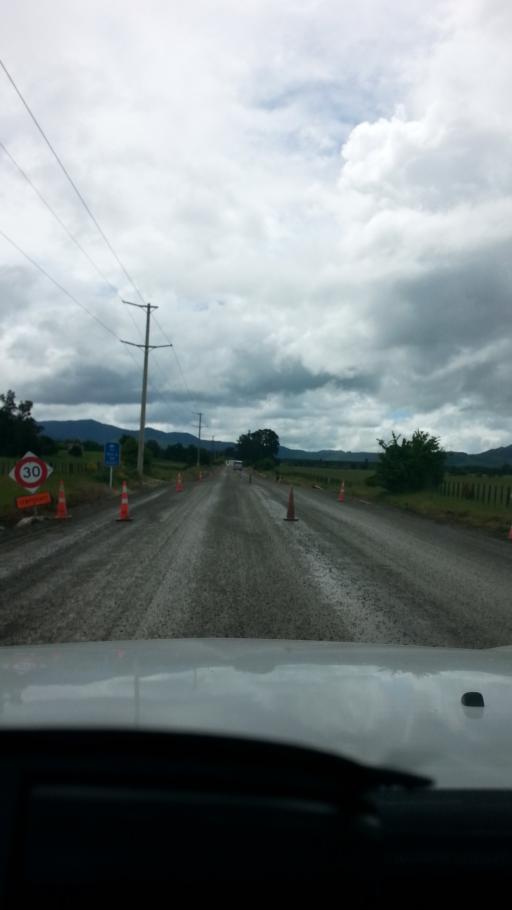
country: NZ
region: Wellington
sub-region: Masterton District
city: Masterton
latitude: -40.8325
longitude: 175.6278
